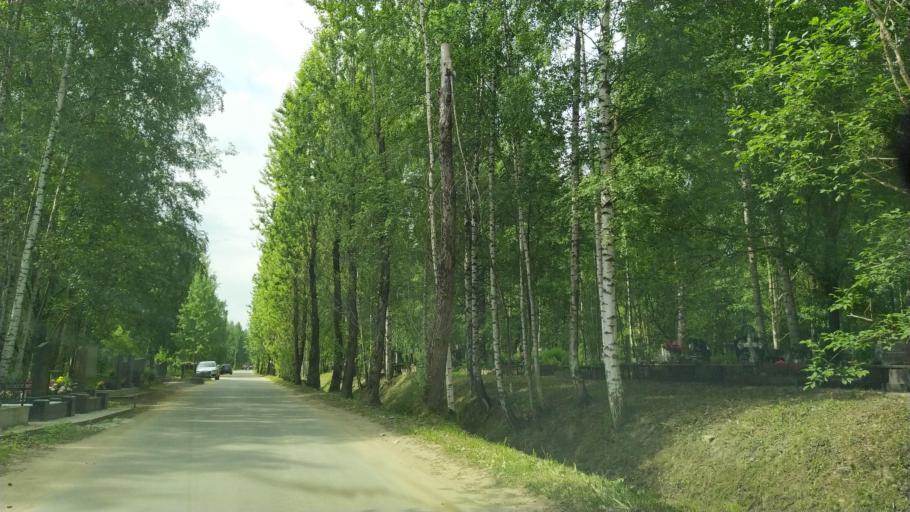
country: RU
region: St.-Petersburg
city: Dachnoye
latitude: 59.7697
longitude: 30.2646
